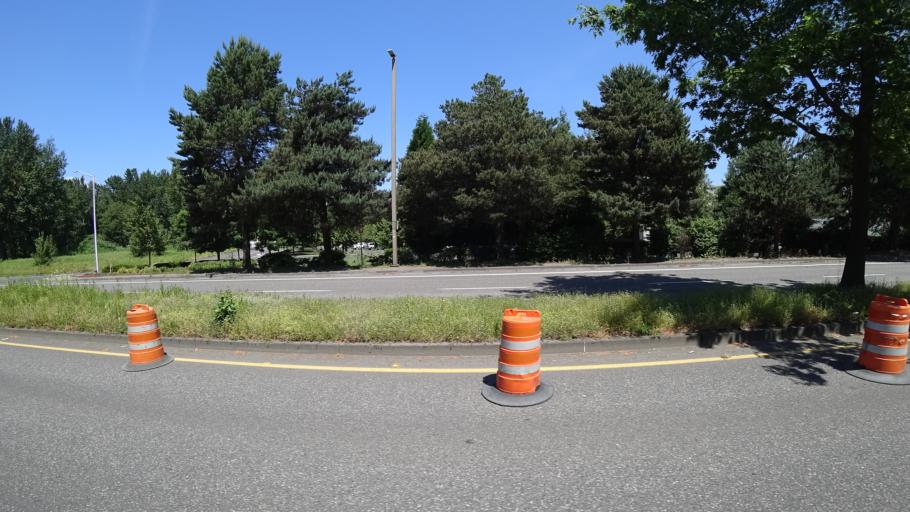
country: US
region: Oregon
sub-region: Multnomah County
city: Fairview
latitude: 45.5556
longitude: -122.4919
